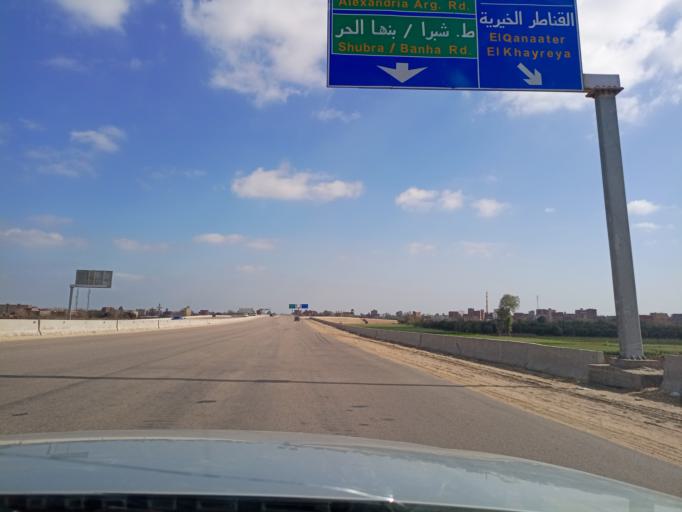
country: EG
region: Muhafazat al Minufiyah
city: Al Bajur
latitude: 30.4023
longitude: 31.0305
